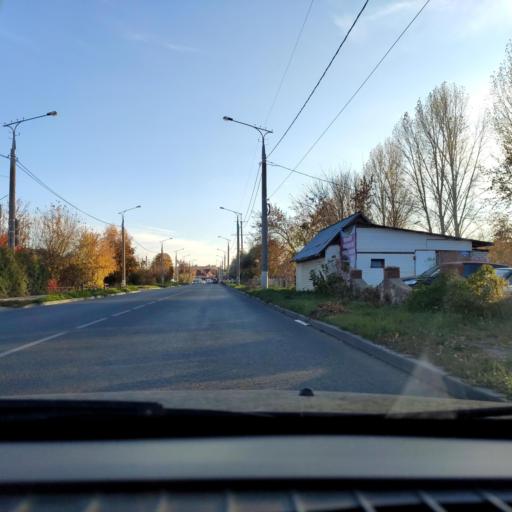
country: RU
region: Samara
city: Tol'yatti
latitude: 53.5130
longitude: 49.3953
